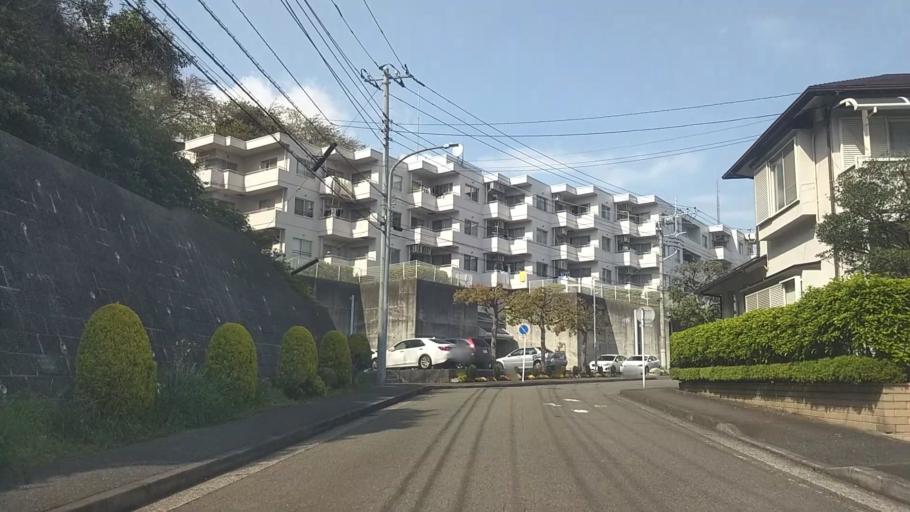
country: JP
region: Kanagawa
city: Kamakura
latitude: 35.3831
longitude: 139.5715
